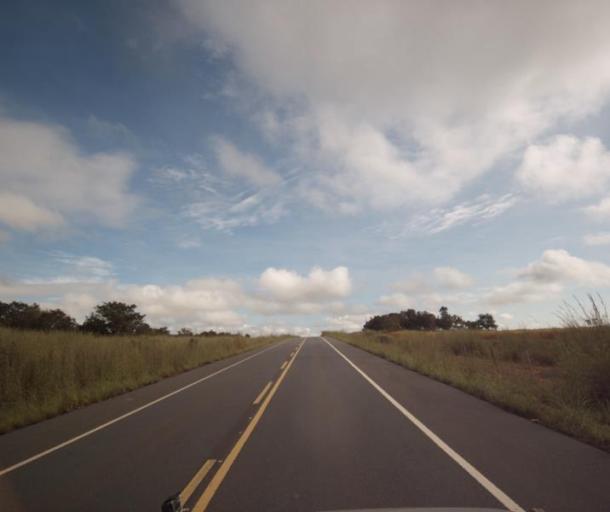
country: BR
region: Goias
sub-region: Barro Alto
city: Barro Alto
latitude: -15.2319
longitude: -48.6936
